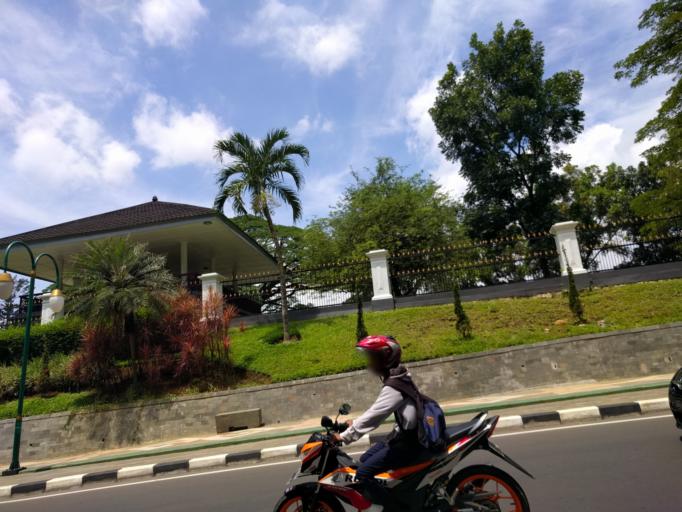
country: ID
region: West Java
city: Bogor
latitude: -6.5934
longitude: 106.7978
